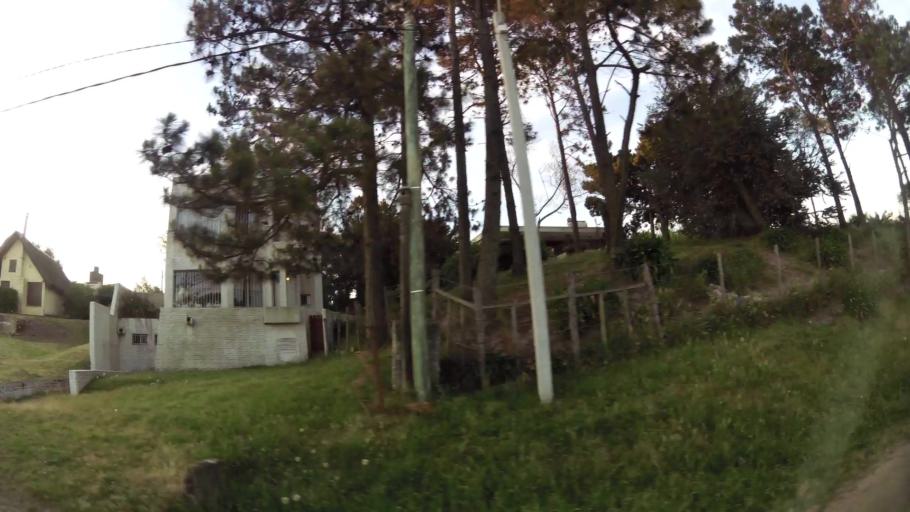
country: UY
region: Canelones
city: Atlantida
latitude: -34.7705
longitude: -55.7740
